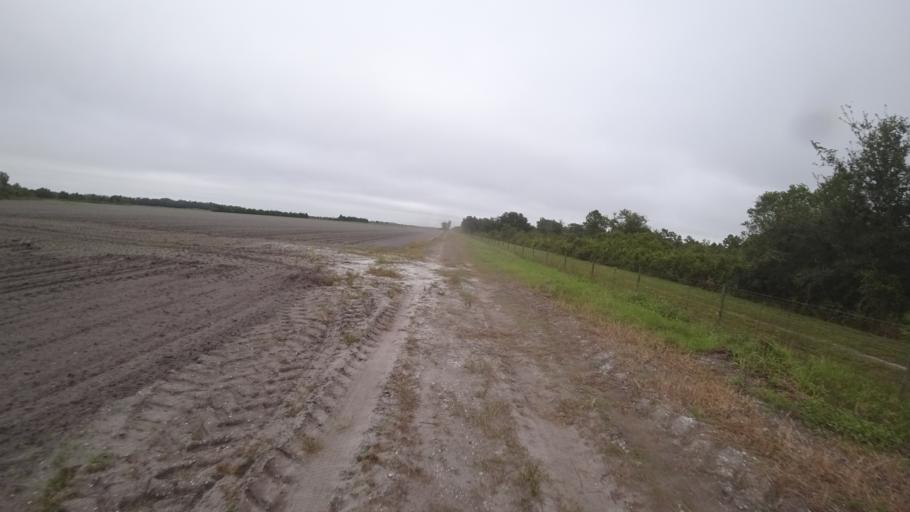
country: US
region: Florida
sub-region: Sarasota County
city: Warm Mineral Springs
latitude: 27.2776
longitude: -82.1346
